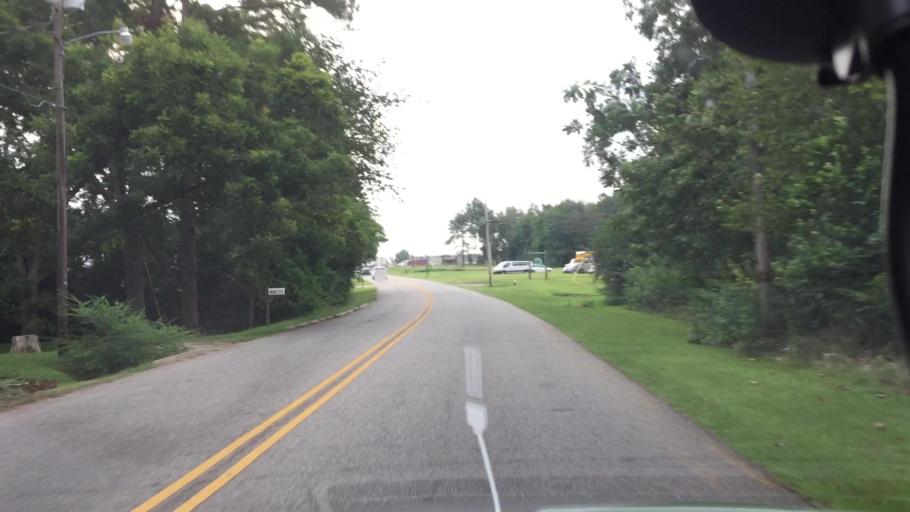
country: US
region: Alabama
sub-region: Coffee County
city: Enterprise
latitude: 31.3164
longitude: -85.8350
